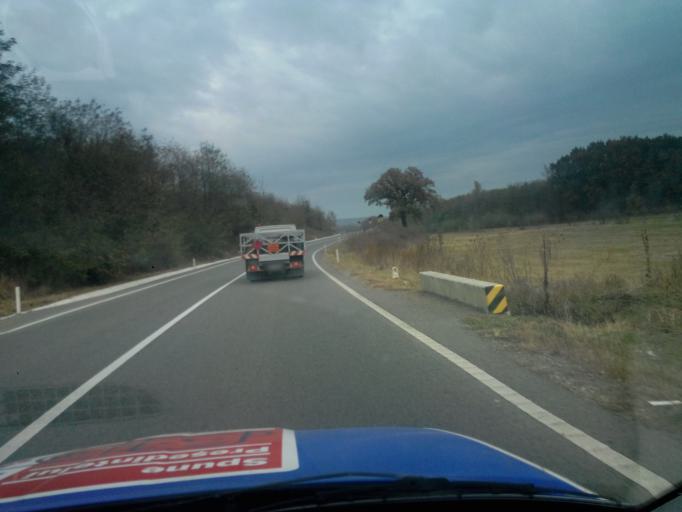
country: RO
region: Vaslui
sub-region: Comuna Tatarani
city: Tatarani
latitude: 46.6643
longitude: 27.9870
